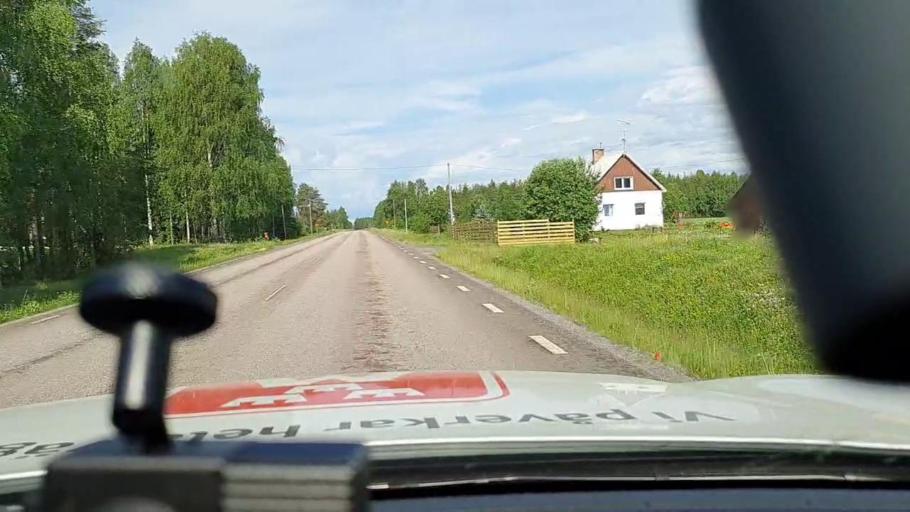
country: SE
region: Norrbotten
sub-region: Alvsbyns Kommun
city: AElvsbyn
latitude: 66.0172
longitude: 21.1523
